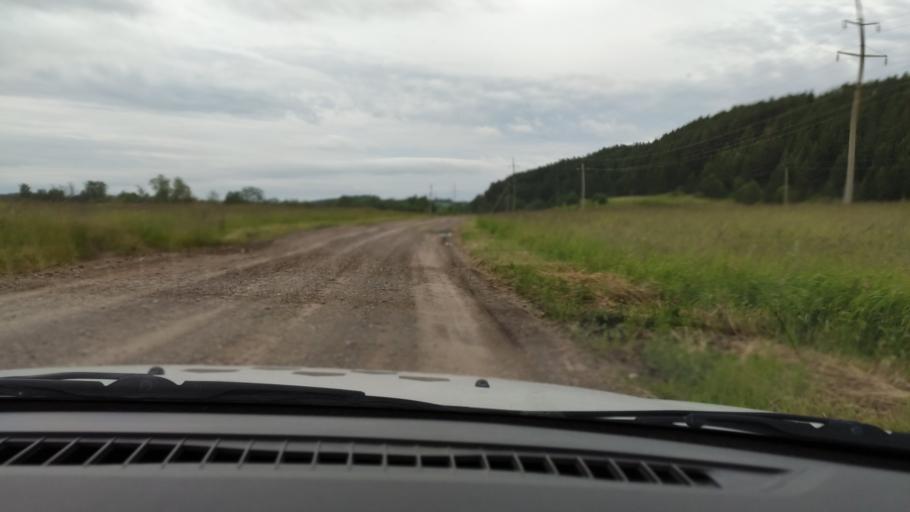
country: RU
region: Perm
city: Orda
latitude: 57.3022
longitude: 56.6334
